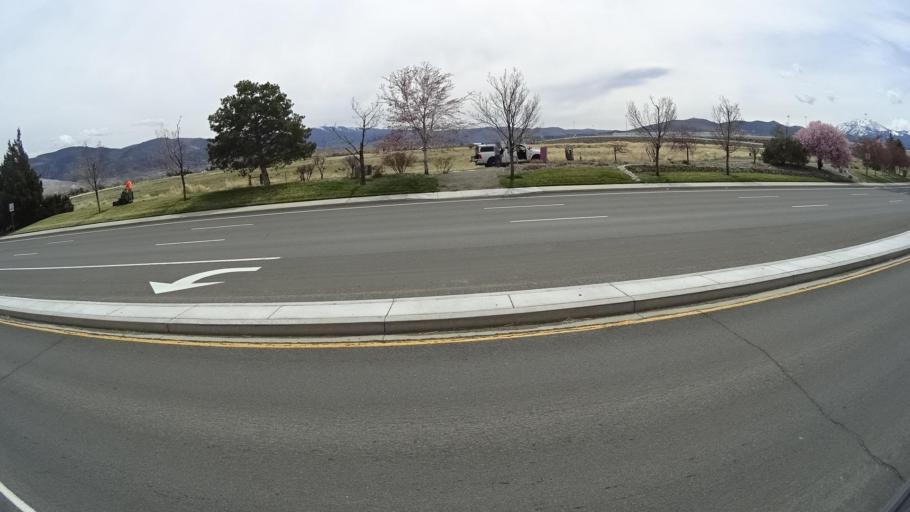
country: US
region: Nevada
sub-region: Washoe County
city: Sparks
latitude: 39.4246
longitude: -119.7474
